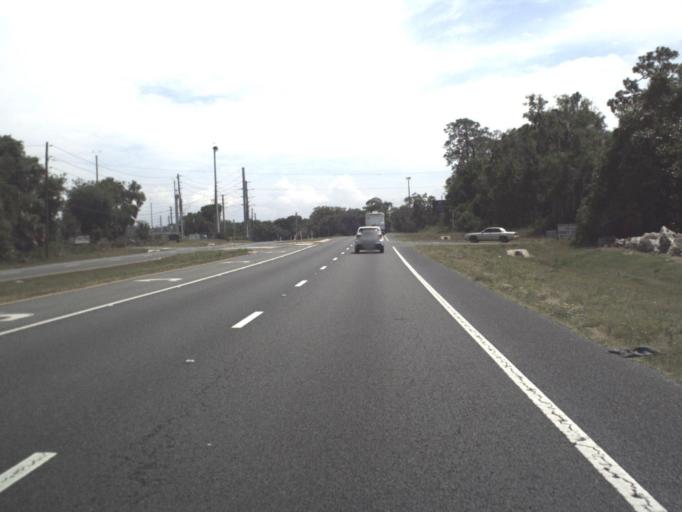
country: US
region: Florida
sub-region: Sumter County
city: Wildwood
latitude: 28.8263
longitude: -81.9915
